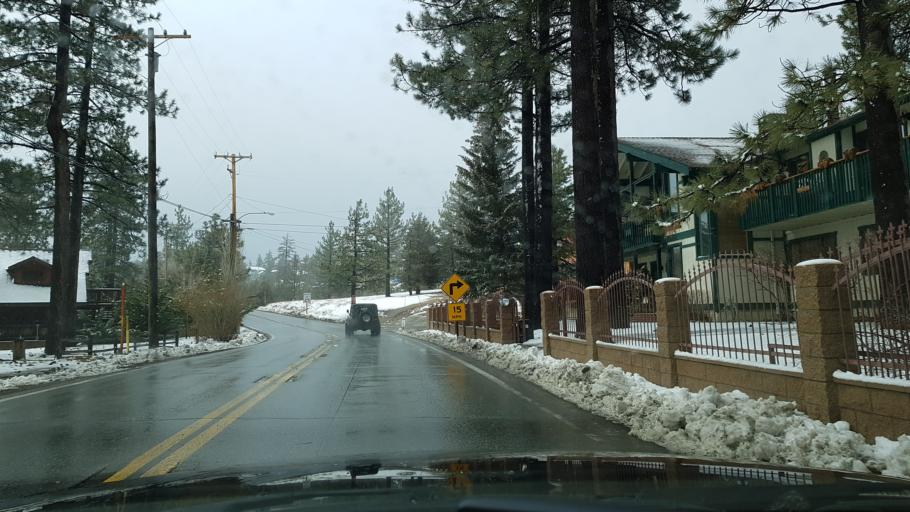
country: US
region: California
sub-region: San Bernardino County
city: Big Bear Lake
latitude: 34.2658
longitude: -116.9395
